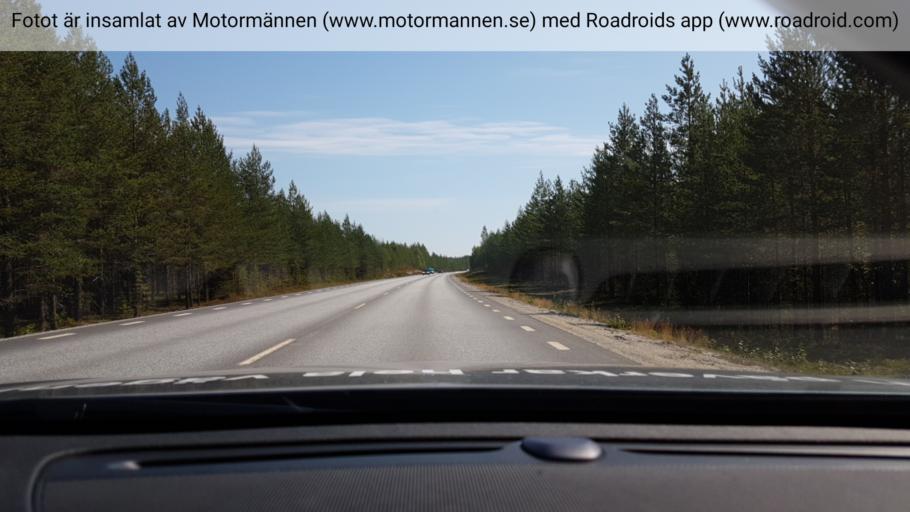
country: SE
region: Vaesterbotten
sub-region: Vindelns Kommun
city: Vindeln
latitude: 64.1583
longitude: 19.8372
